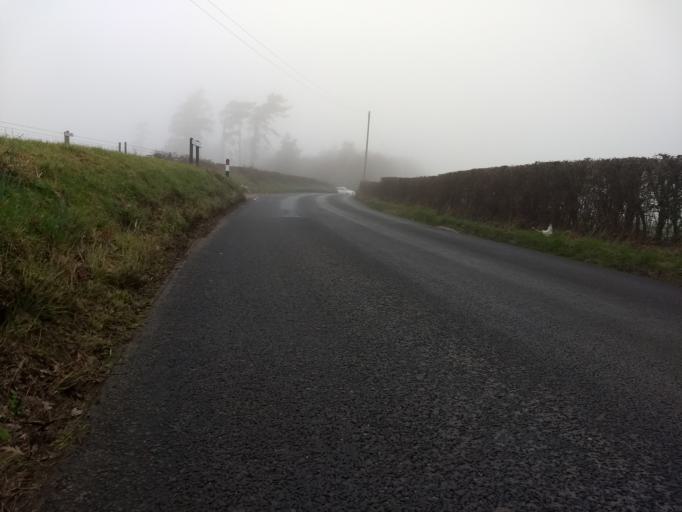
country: GB
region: England
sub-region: Isle of Wight
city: Newchurch
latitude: 50.7008
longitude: -1.2383
